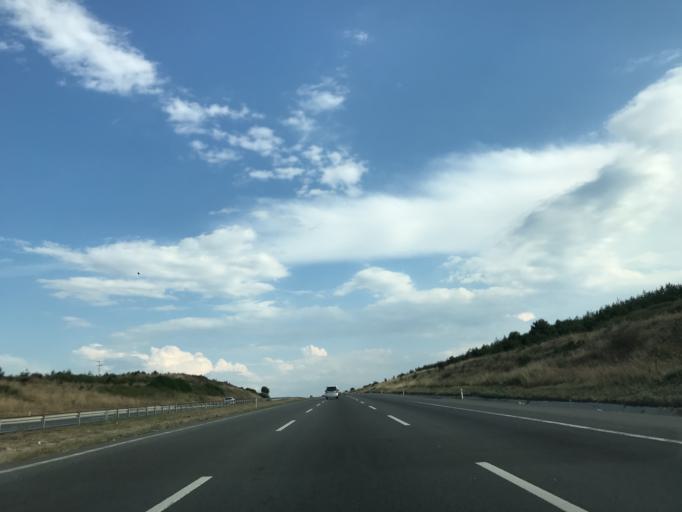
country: TR
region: Bolu
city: Yenicaga
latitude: 40.7609
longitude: 32.0612
